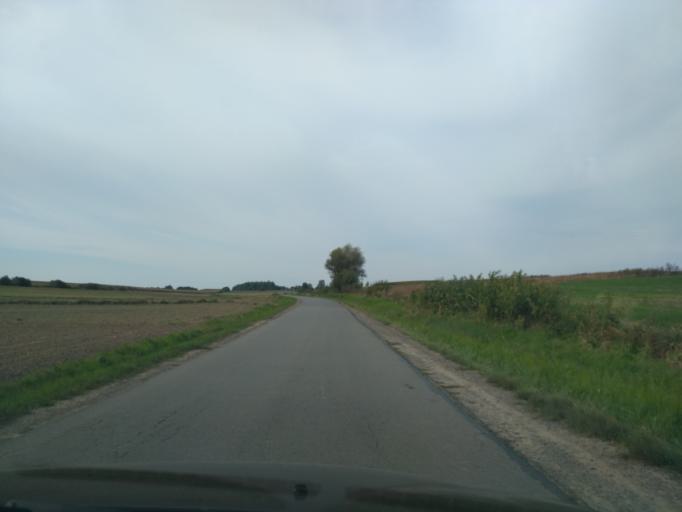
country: PL
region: Subcarpathian Voivodeship
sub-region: Powiat rzeszowski
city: Zglobien
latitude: 50.0197
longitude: 21.8472
